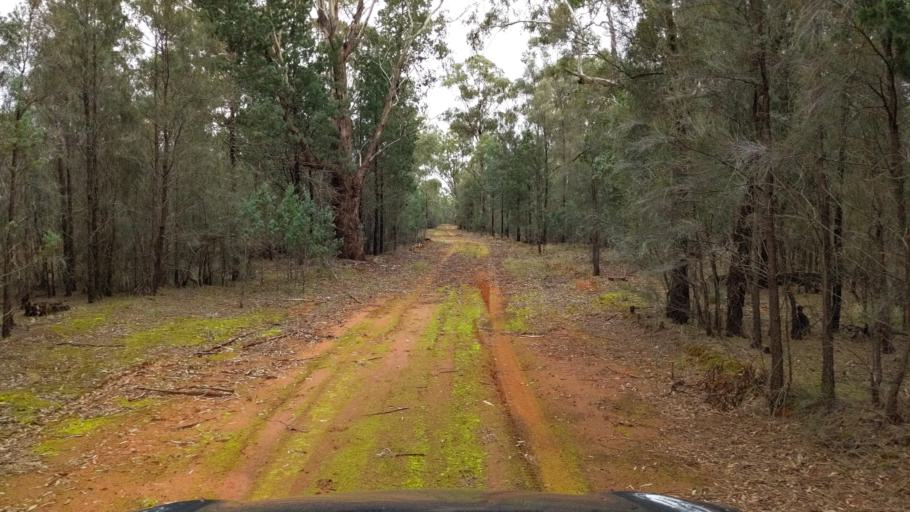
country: AU
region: New South Wales
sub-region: Coolamon
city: Coolamon
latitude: -34.8394
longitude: 146.9339
